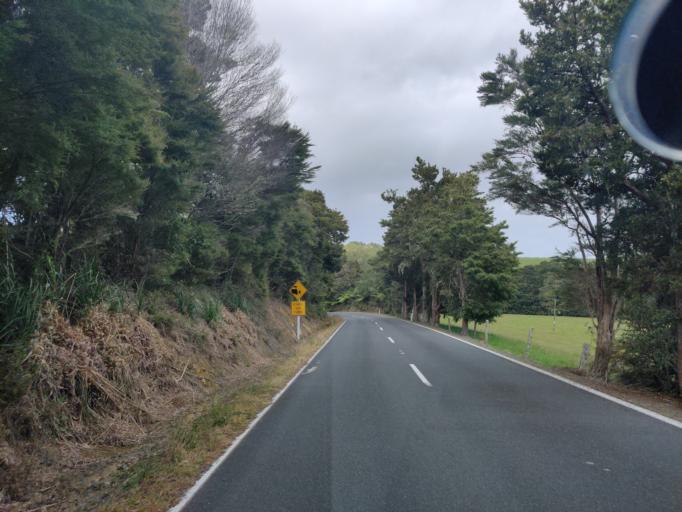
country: NZ
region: Northland
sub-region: Whangarei
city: Ngunguru
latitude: -35.5769
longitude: 174.4016
